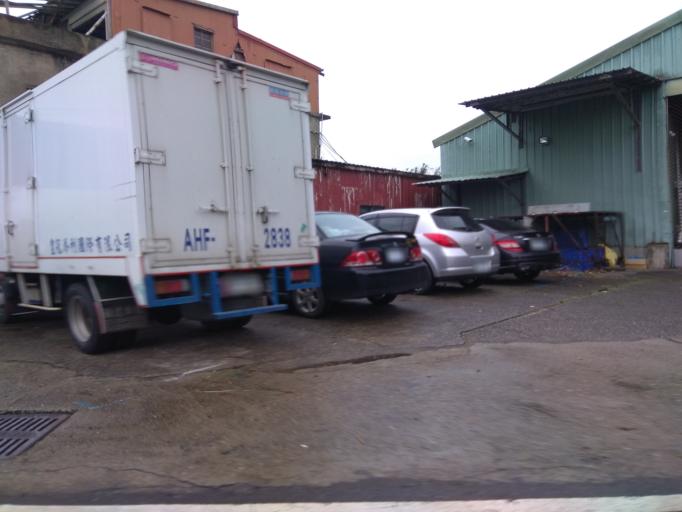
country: TW
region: Taiwan
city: Taoyuan City
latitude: 25.0371
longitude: 121.2203
